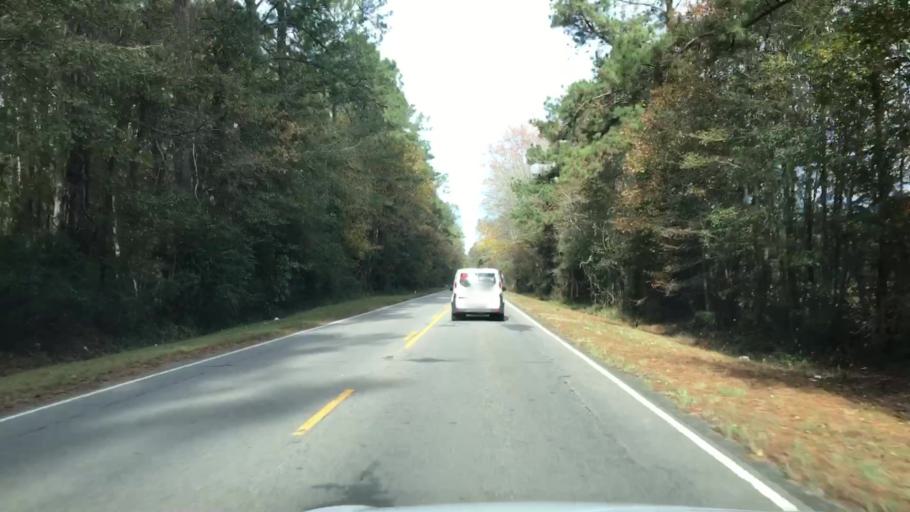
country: US
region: South Carolina
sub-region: Colleton County
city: Walterboro
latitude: 32.8878
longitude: -80.6238
